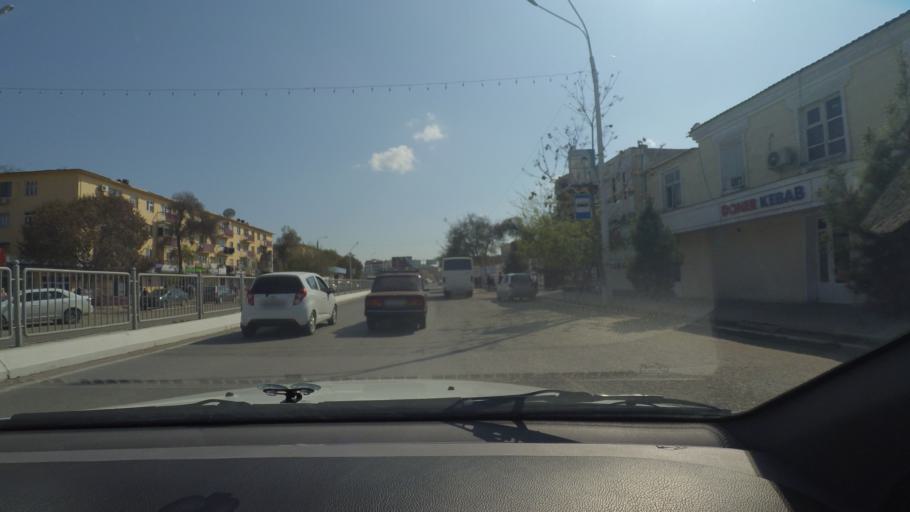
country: UZ
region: Bukhara
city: Bukhara
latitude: 39.7642
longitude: 64.4305
